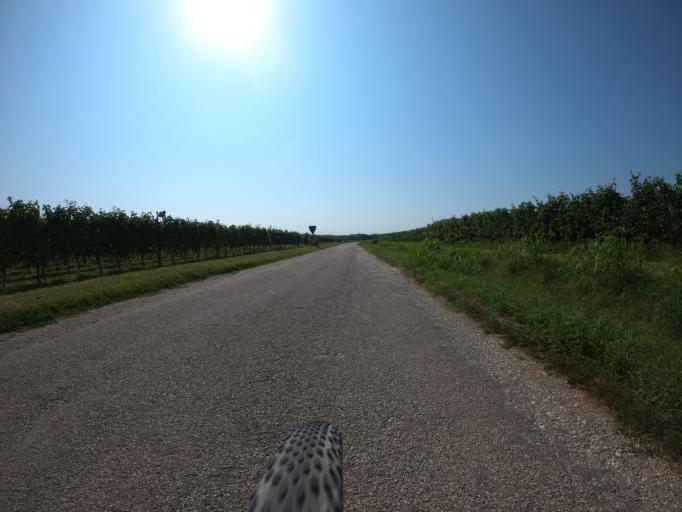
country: IT
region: Veneto
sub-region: Provincia di Verona
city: Costermano
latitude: 45.5900
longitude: 10.7572
